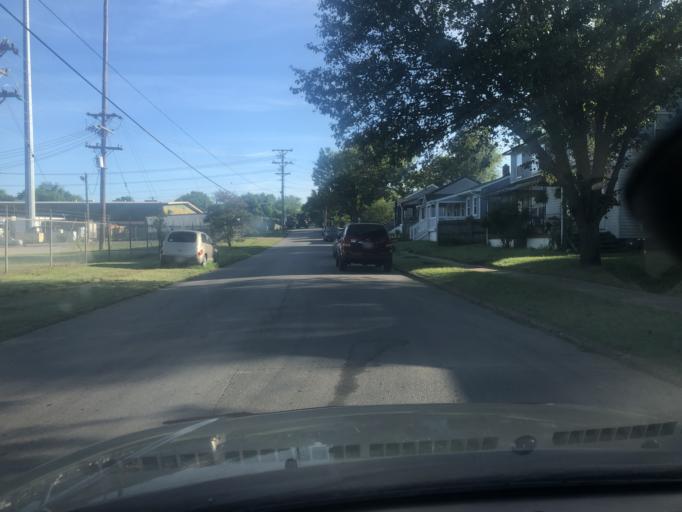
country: US
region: Tennessee
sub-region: Davidson County
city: Lakewood
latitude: 36.2576
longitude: -86.6509
